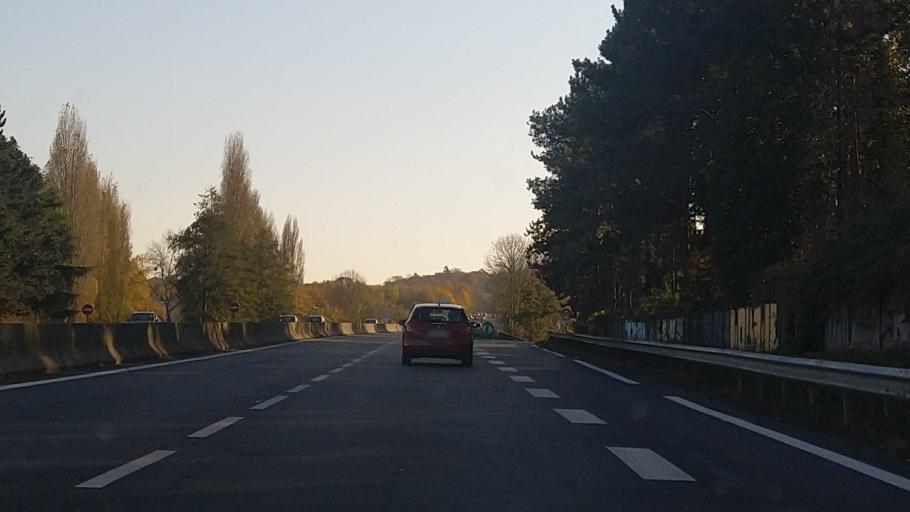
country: FR
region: Ile-de-France
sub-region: Departement du Val-d'Oise
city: Moisselles
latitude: 49.0366
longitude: 2.3452
